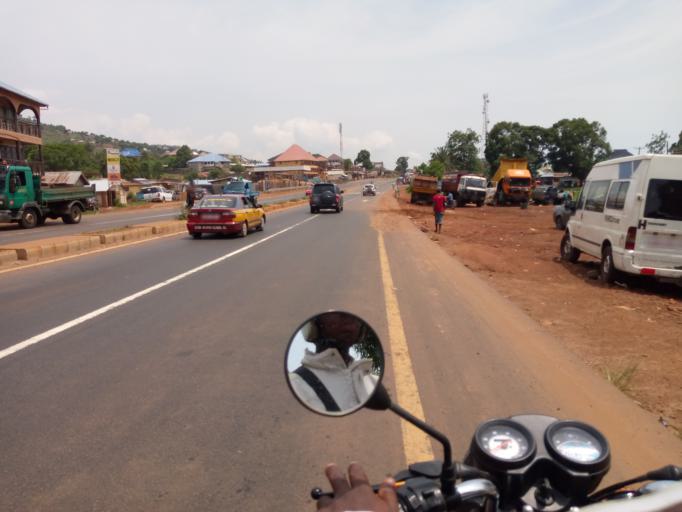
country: SL
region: Western Area
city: Waterloo
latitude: 8.3682
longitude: -13.0910
